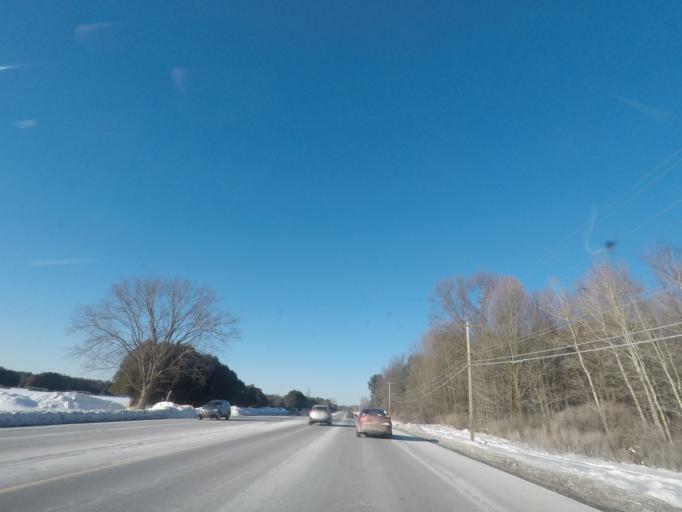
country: US
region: New York
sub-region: Saratoga County
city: Saratoga Springs
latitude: 43.0505
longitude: -73.7882
